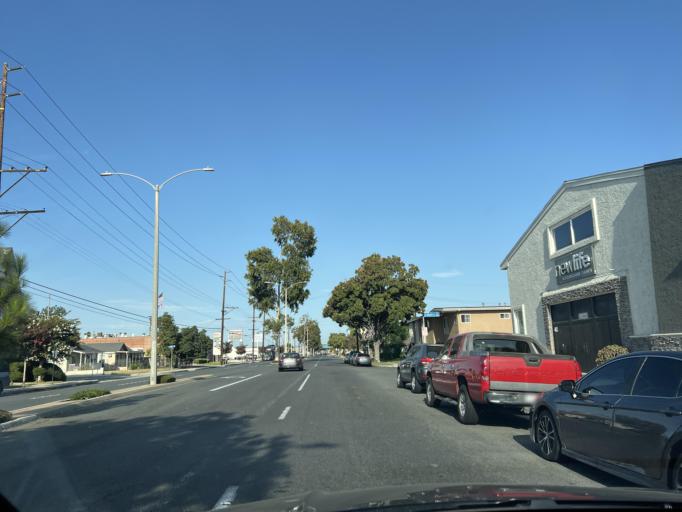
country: US
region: California
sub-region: Los Angeles County
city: Norwalk
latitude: 33.9022
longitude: -118.0707
